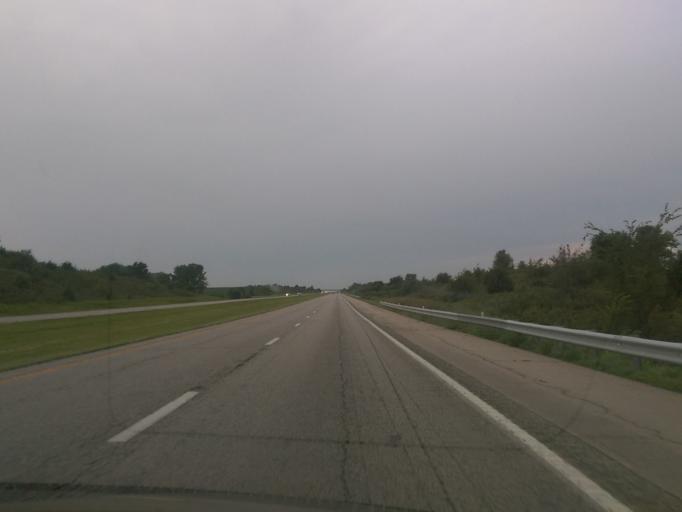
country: US
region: Missouri
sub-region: Holt County
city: Oregon
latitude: 40.0179
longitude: -95.0904
